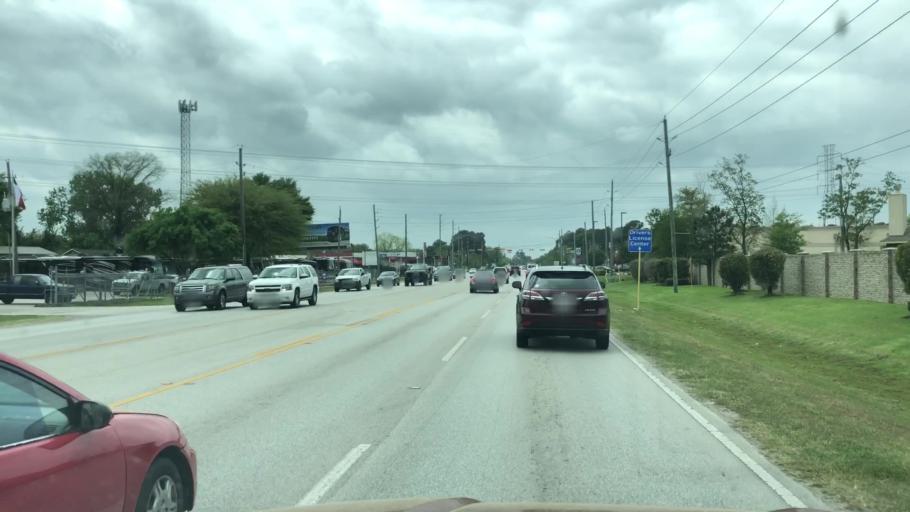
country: US
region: Texas
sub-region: Harris County
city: Spring
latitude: 30.0518
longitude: -95.4907
